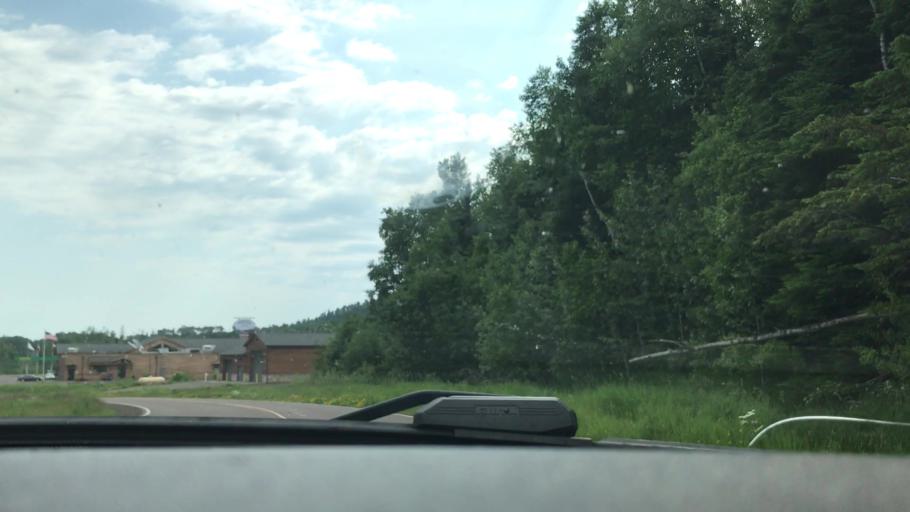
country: CA
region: Ontario
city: Neebing
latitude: 47.9557
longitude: -89.6937
